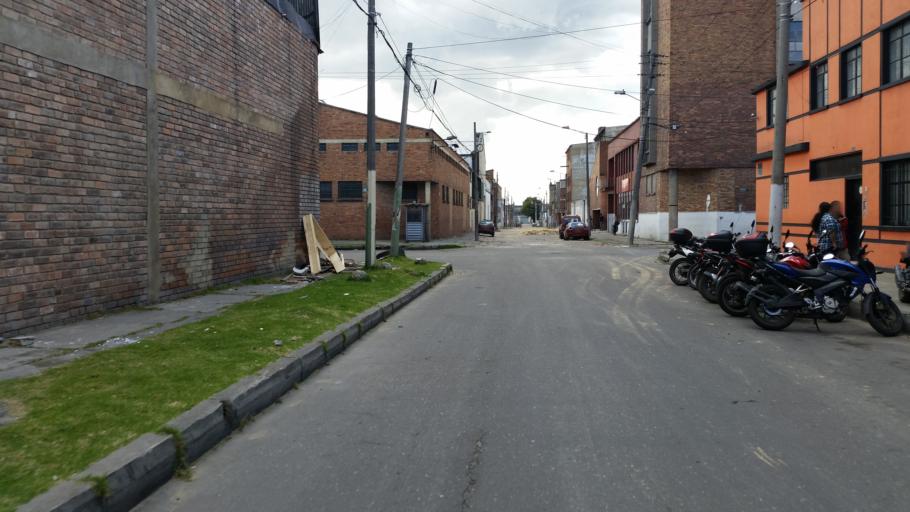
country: CO
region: Bogota D.C.
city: Bogota
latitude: 4.6181
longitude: -74.0942
